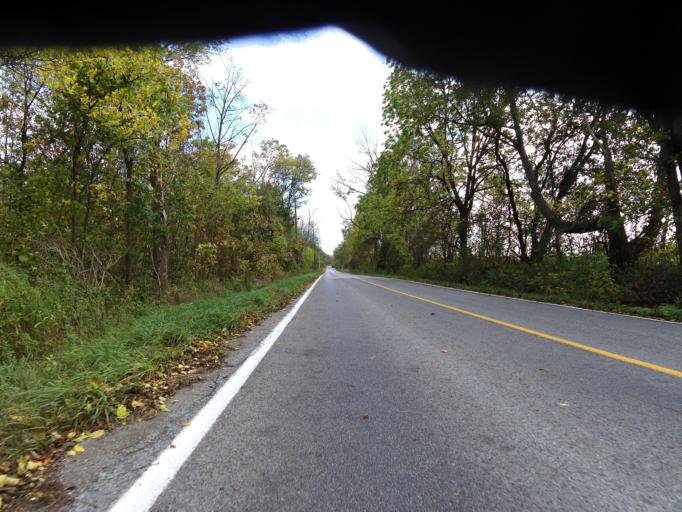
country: CA
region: Ontario
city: Burlington
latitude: 43.3633
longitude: -79.8827
